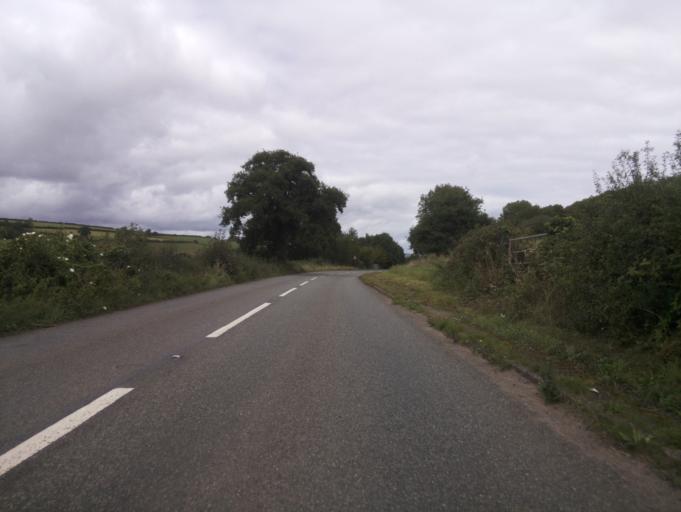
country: GB
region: England
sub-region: Devon
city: Cullompton
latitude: 50.8343
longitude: -3.3925
